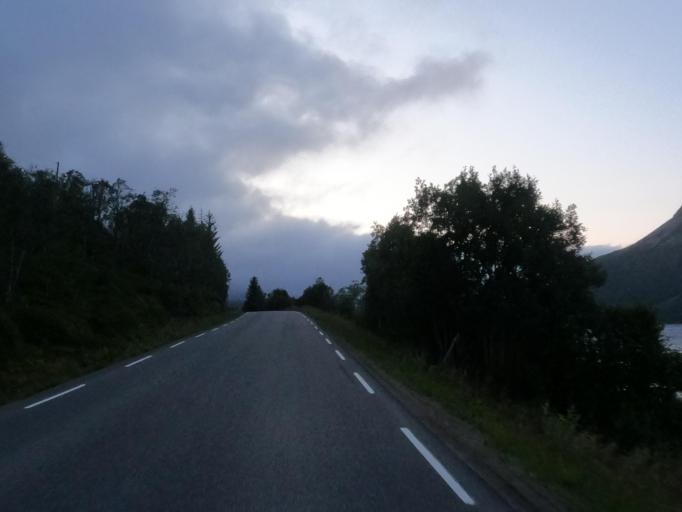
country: NO
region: Nordland
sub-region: Lodingen
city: Lodingen
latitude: 68.5900
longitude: 15.7906
